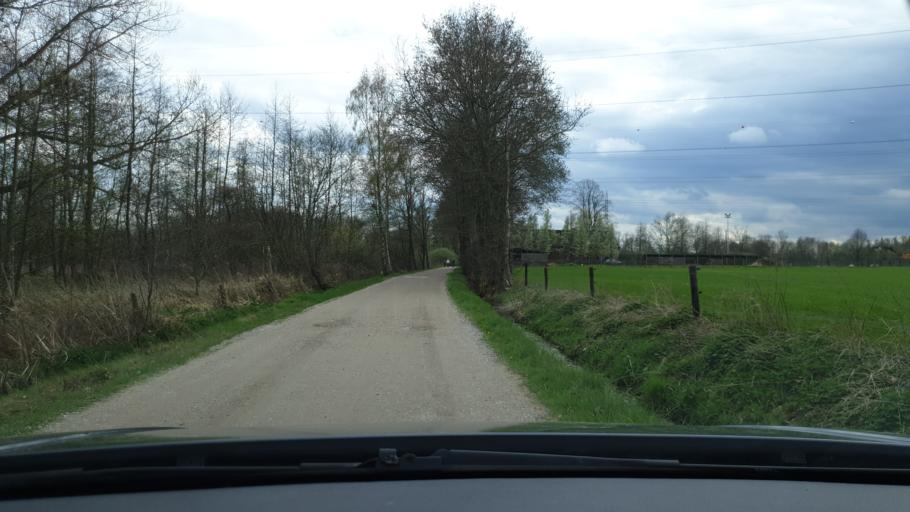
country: BE
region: Flanders
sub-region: Provincie Antwerpen
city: Geel
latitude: 51.1277
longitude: 4.9865
